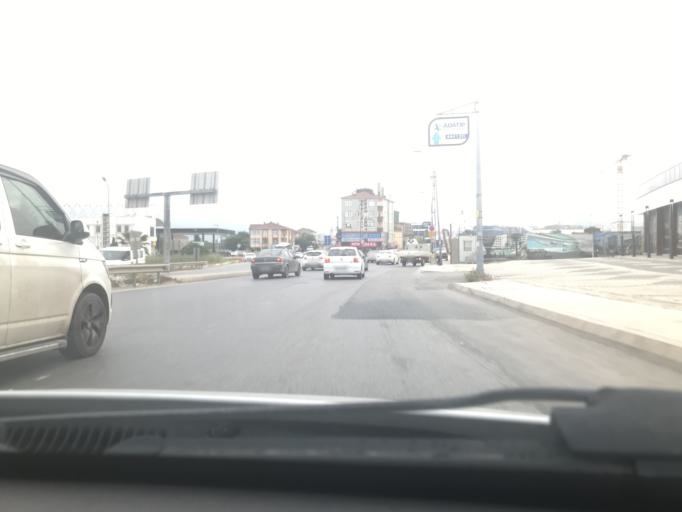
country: TR
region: Istanbul
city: Sultanbeyli
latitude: 40.9303
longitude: 29.3271
